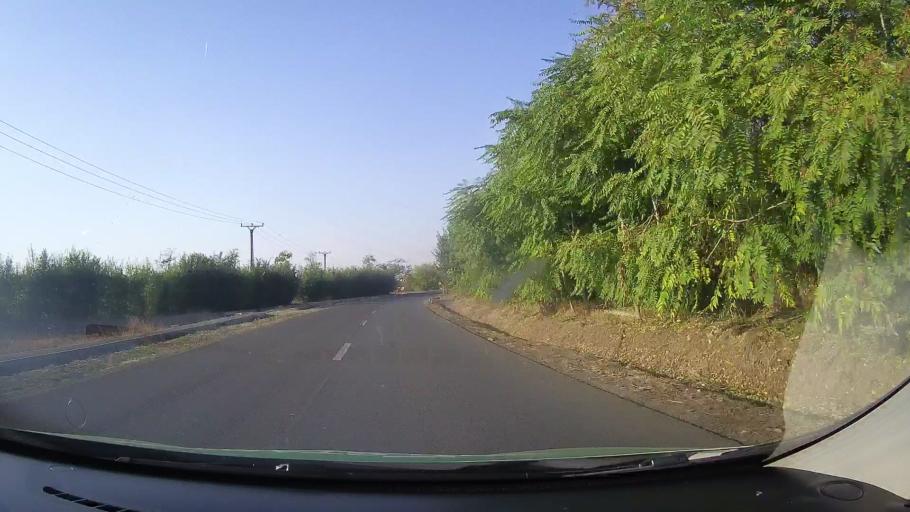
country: RO
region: Arad
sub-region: Comuna Siria
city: Siria
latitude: 46.2470
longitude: 21.6297
